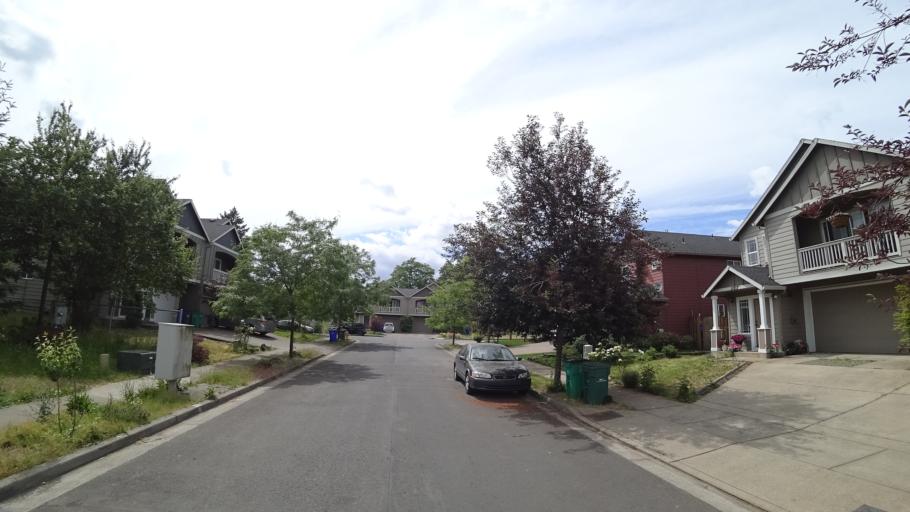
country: US
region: Oregon
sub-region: Multnomah County
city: Lents
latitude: 45.4840
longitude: -122.5476
